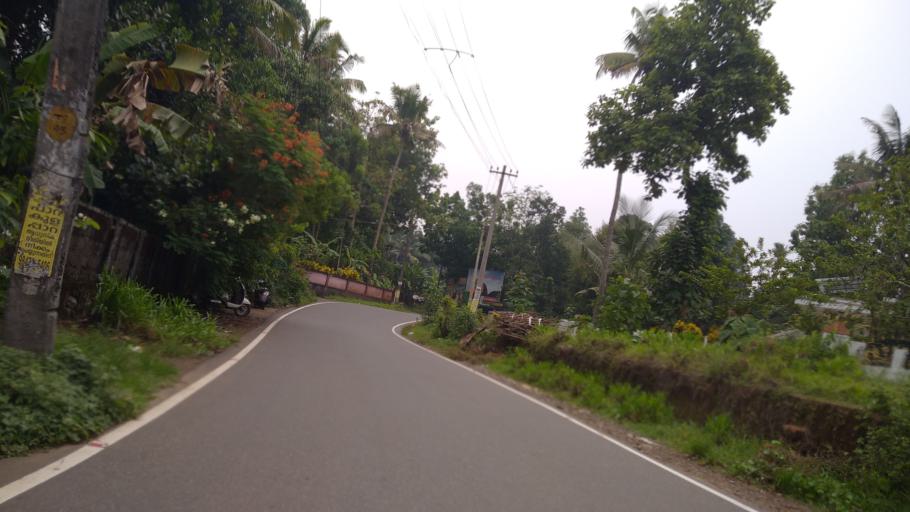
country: IN
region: Kerala
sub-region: Ernakulam
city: Perumpavur
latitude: 10.1199
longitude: 76.5329
